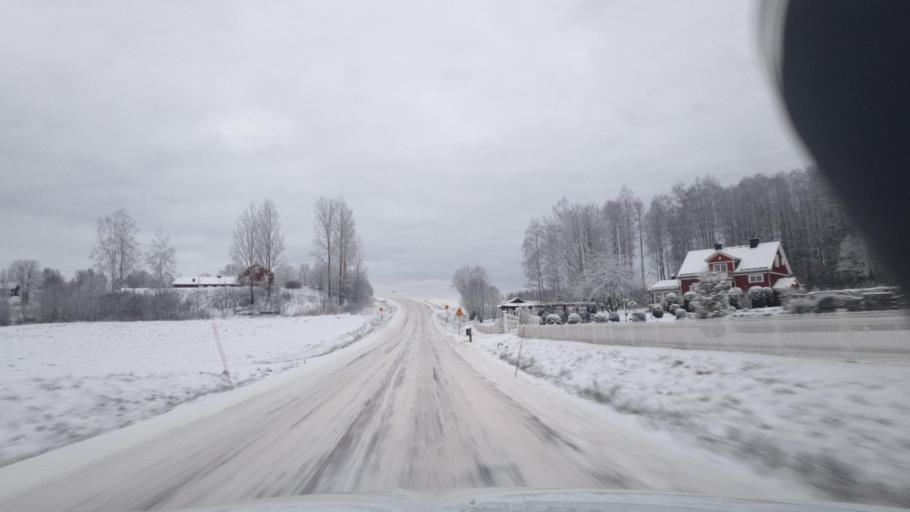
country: SE
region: Vaermland
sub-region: Eda Kommun
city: Charlottenberg
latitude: 59.7735
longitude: 12.1622
